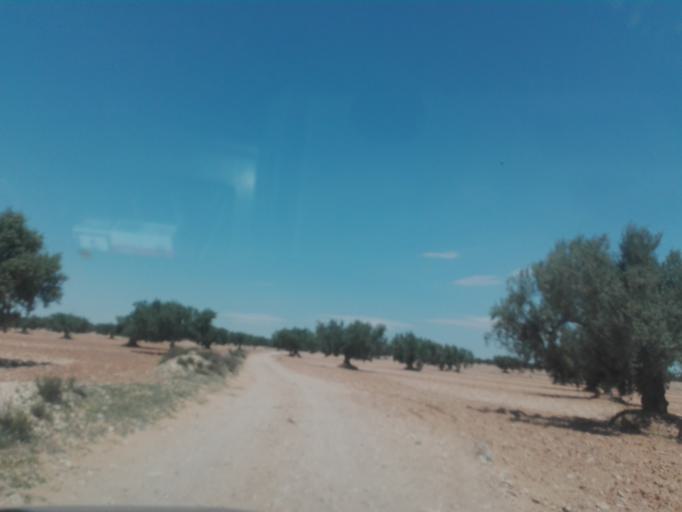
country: TN
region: Safaqis
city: Sfax
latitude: 34.6640
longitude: 10.6061
